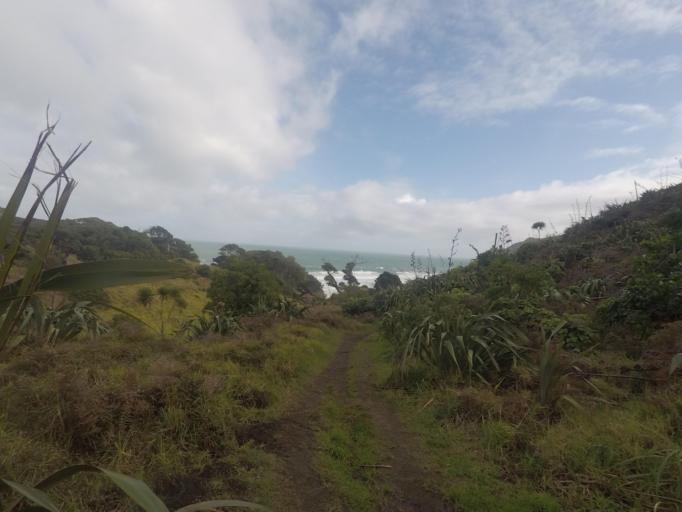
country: NZ
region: Auckland
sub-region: Auckland
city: Muriwai Beach
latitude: -36.8873
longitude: 174.4405
